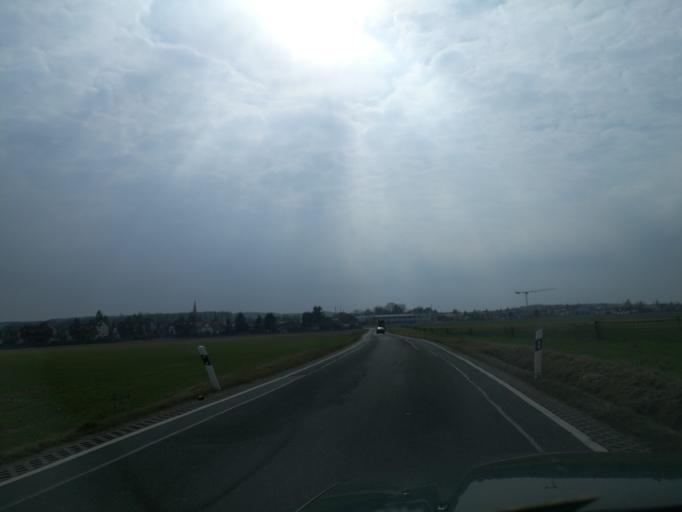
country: DE
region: Bavaria
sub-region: Regierungsbezirk Mittelfranken
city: Obermichelbach
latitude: 49.4955
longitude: 10.9307
